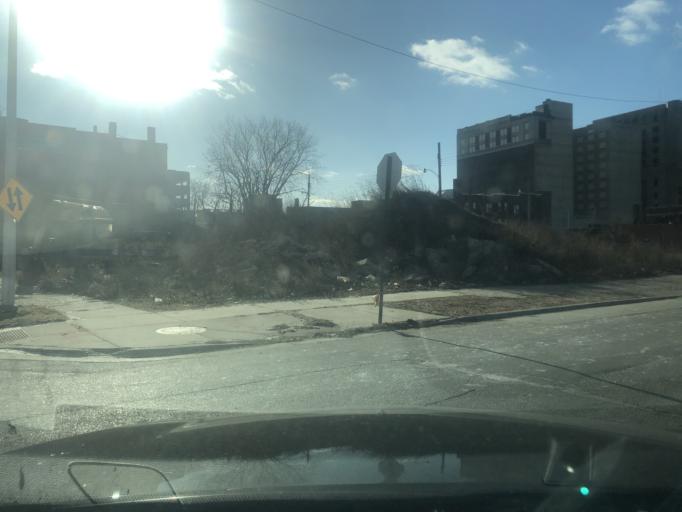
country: US
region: Michigan
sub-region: Wayne County
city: Detroit
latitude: 42.3435
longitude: -83.0581
